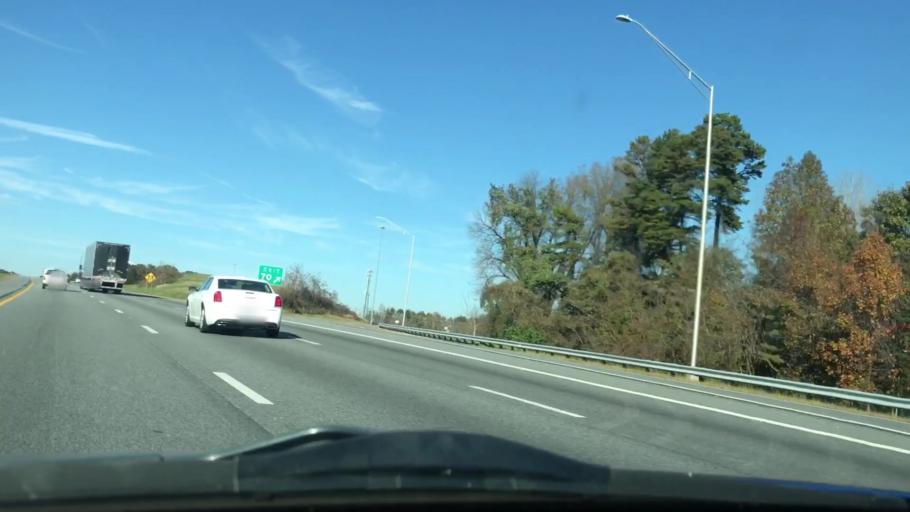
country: US
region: North Carolina
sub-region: Guilford County
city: High Point
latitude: 35.9613
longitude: -79.9743
